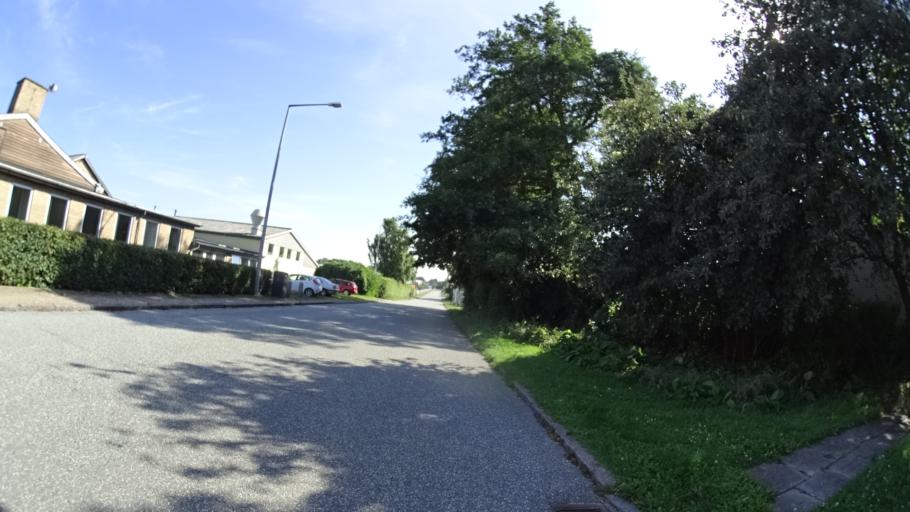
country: DK
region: Central Jutland
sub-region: Arhus Kommune
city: Stavtrup
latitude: 56.1463
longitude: 10.1473
